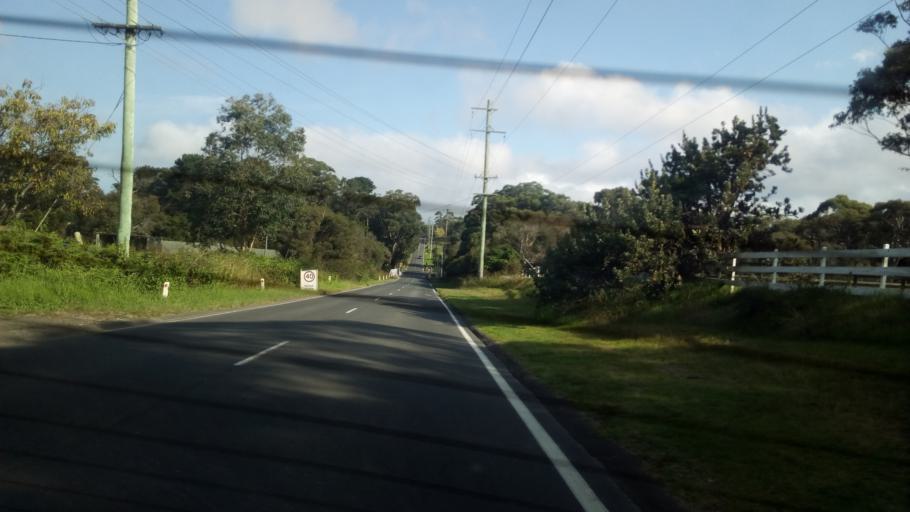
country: AU
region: New South Wales
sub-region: Wollongong
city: Helensburgh
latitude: -34.2059
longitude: 150.9789
